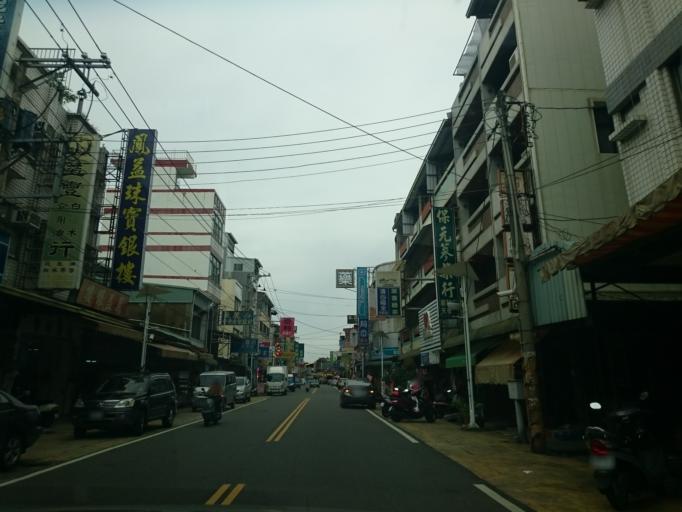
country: TW
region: Taiwan
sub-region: Nantou
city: Nantou
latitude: 23.8370
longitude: 120.7022
